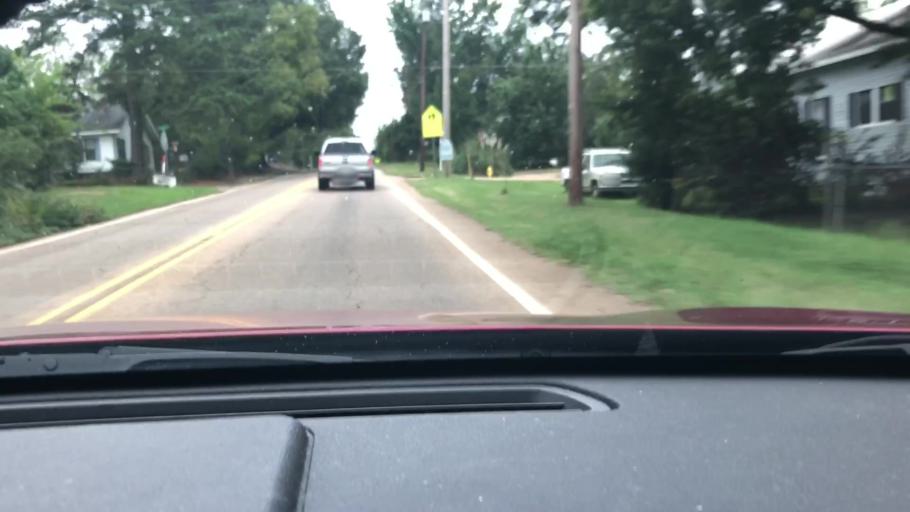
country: US
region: Arkansas
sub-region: Lafayette County
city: Stamps
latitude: 33.3656
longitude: -93.4968
